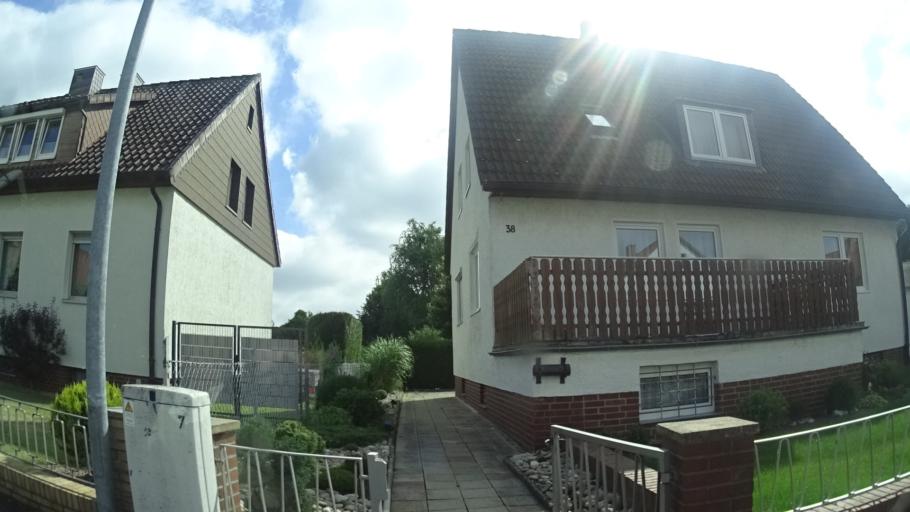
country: DE
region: Lower Saxony
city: Harsum
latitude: 52.1968
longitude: 9.9721
